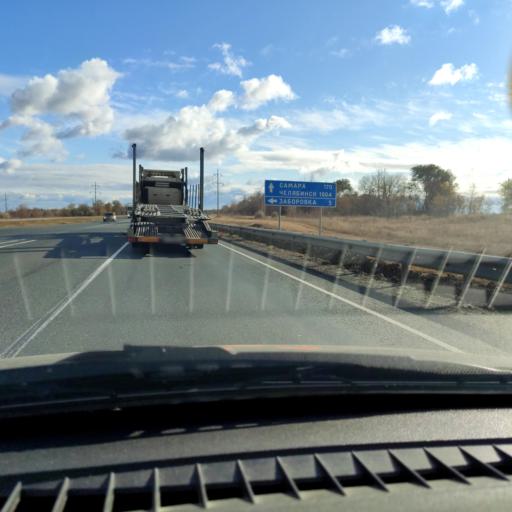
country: RU
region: Samara
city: Varlamovo
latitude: 53.1948
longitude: 48.3239
